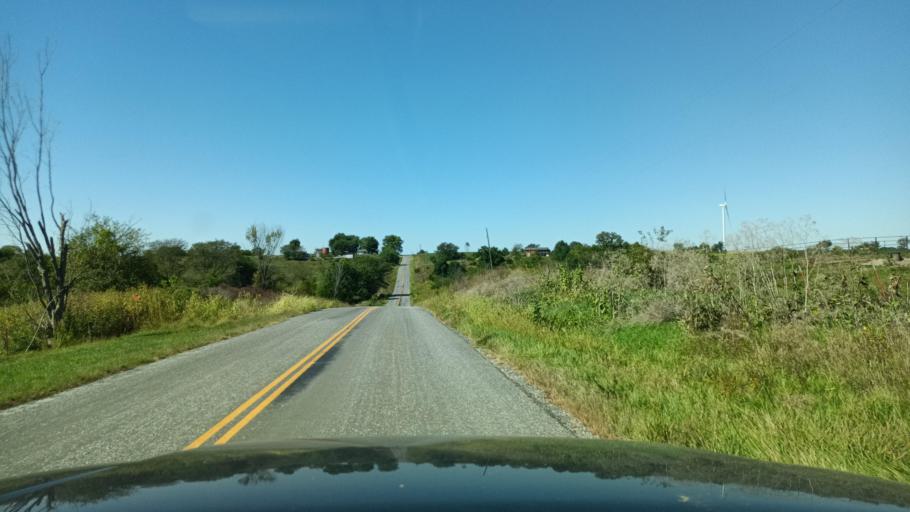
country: US
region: Missouri
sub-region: Adair County
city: Kirksville
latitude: 40.3305
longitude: -92.5172
